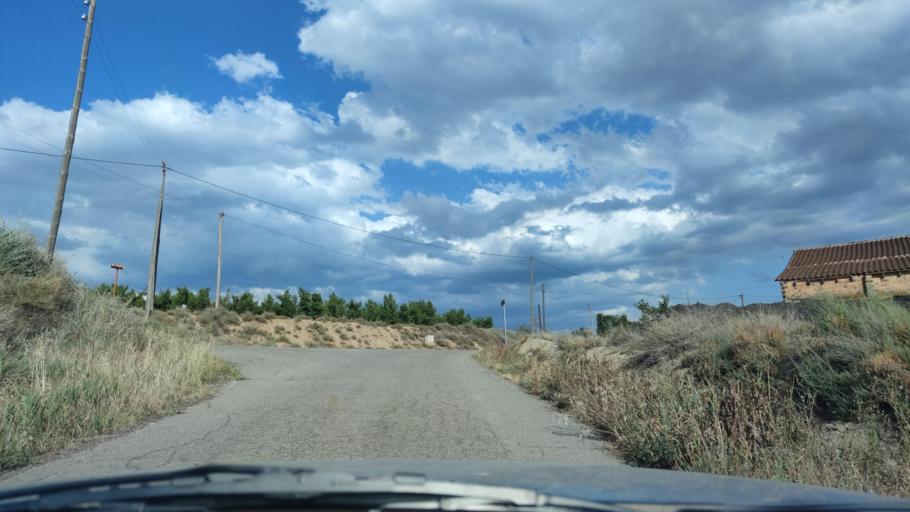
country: ES
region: Catalonia
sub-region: Provincia de Lleida
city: Alpicat
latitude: 41.6316
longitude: 0.5614
